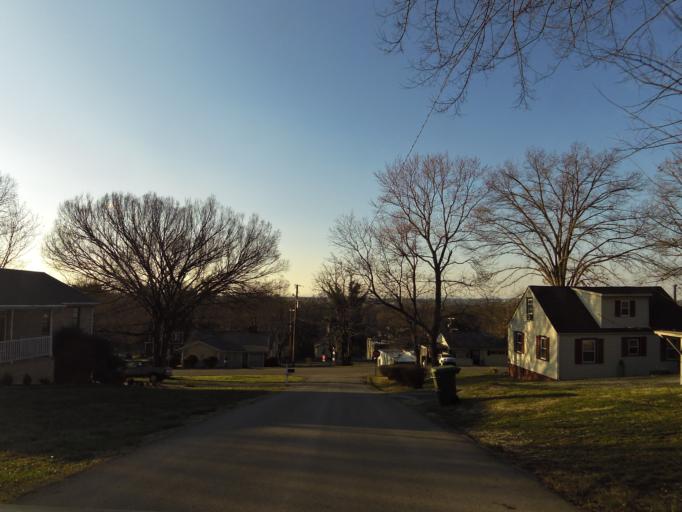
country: US
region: Tennessee
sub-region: Blount County
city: Maryville
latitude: 35.7665
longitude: -83.9587
